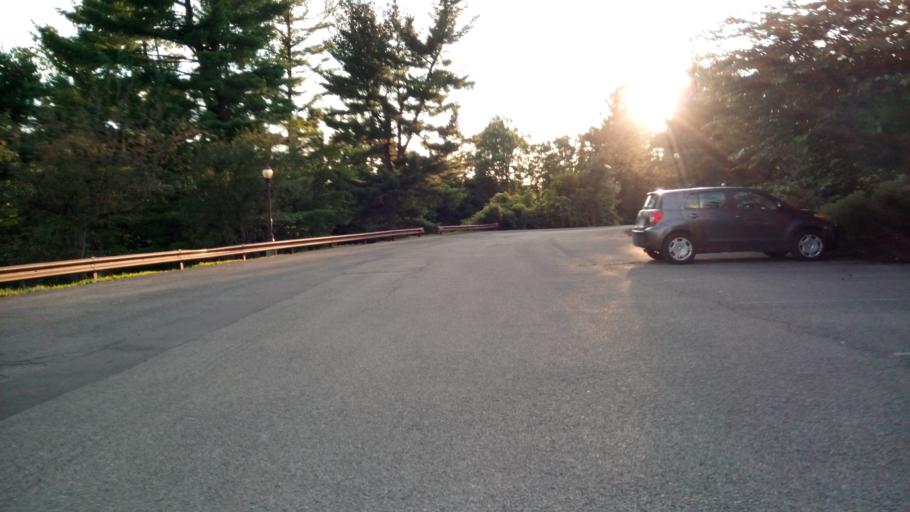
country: US
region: New York
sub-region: Chemung County
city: West Elmira
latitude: 42.0821
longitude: -76.8488
